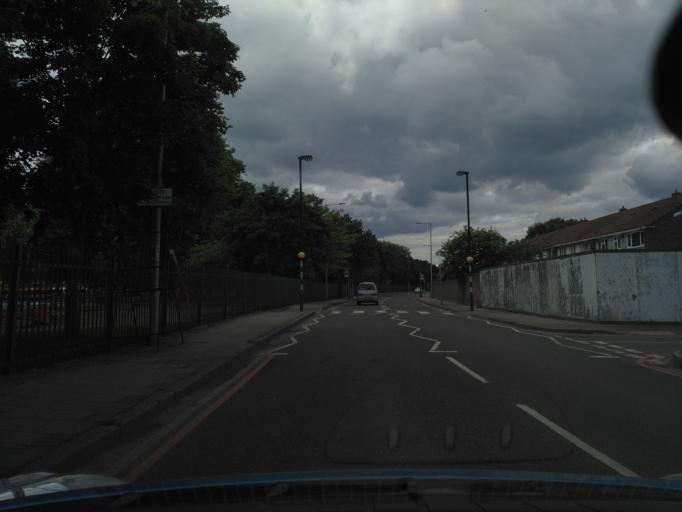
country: GB
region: England
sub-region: Greater London
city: Woolwich
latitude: 51.5008
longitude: 0.0688
